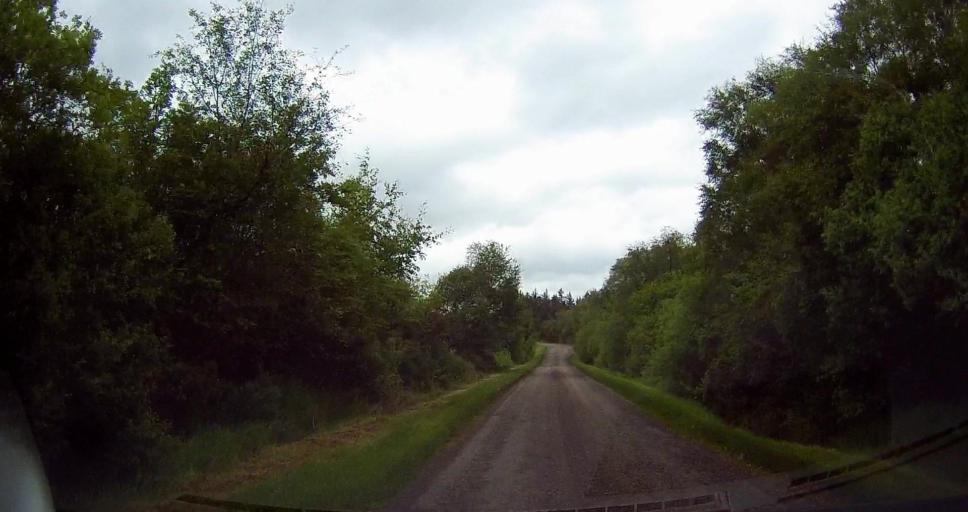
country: GB
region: Scotland
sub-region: Highland
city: Evanton
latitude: 58.0730
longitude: -4.4615
